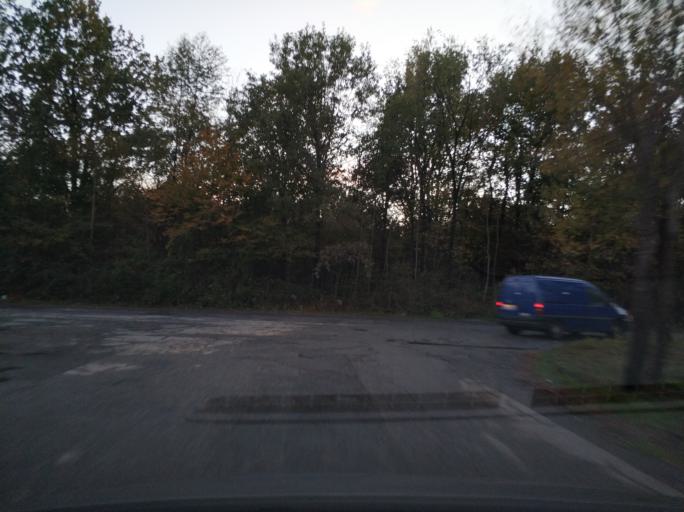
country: IT
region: Piedmont
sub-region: Provincia di Torino
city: Robassomero
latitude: 45.1750
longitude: 7.5905
